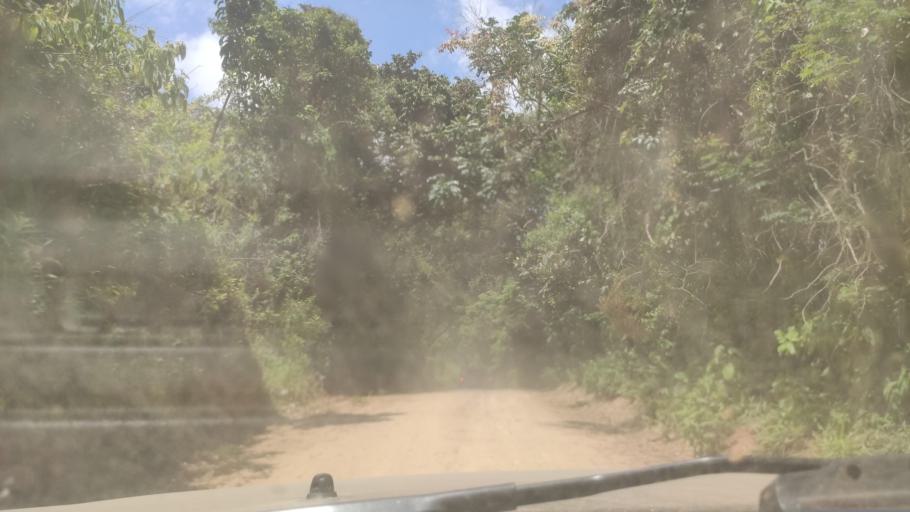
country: BR
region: Minas Gerais
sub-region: Cambui
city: Cambui
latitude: -22.6674
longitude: -45.9490
